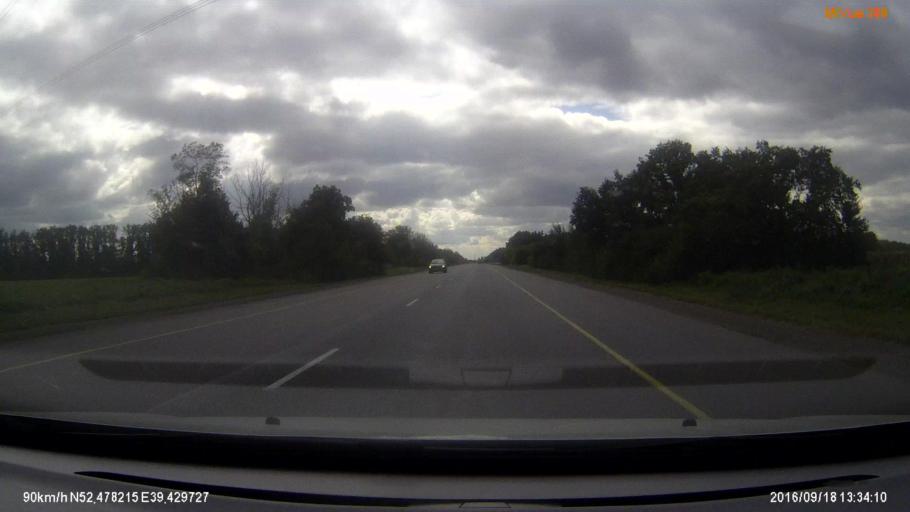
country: RU
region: Lipetsk
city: Borinskoye
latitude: 52.4534
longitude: 39.3755
